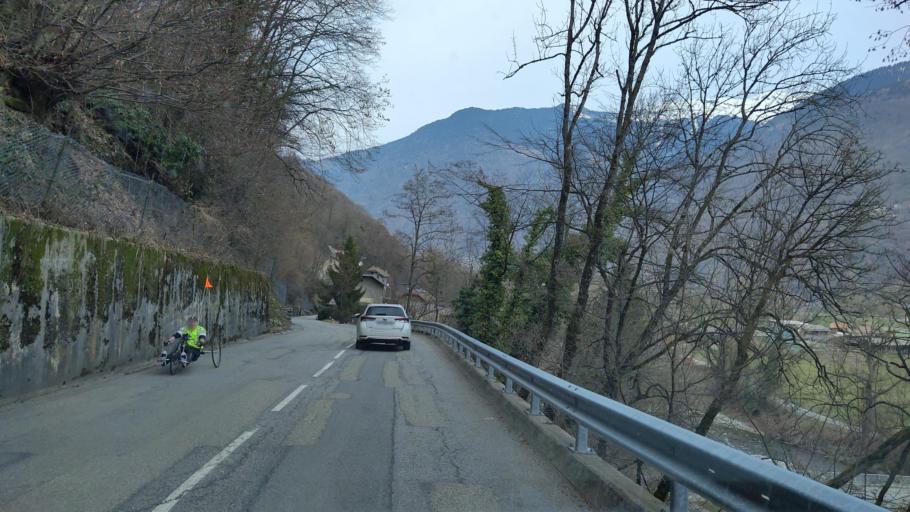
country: FR
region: Rhone-Alpes
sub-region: Departement de la Savoie
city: La Bathie
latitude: 45.6266
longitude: 6.4345
